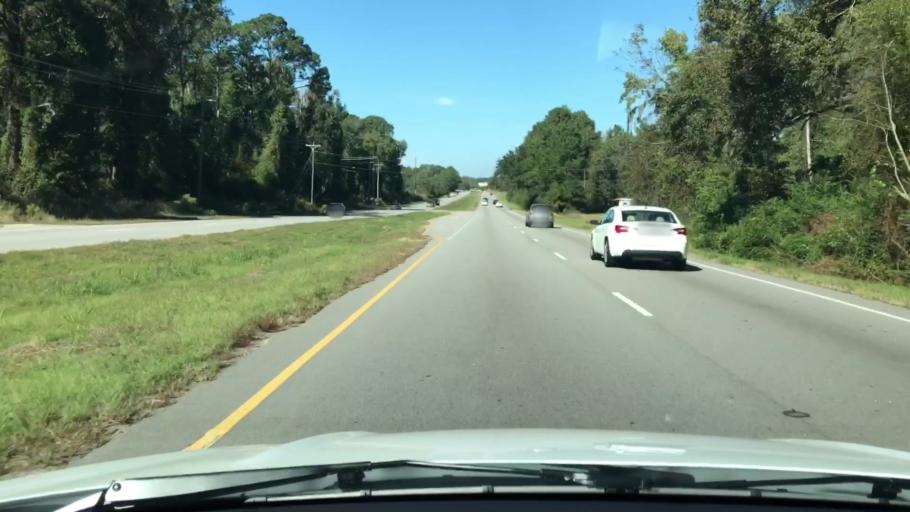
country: US
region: South Carolina
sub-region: Beaufort County
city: Laurel Bay
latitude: 32.4970
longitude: -80.7430
